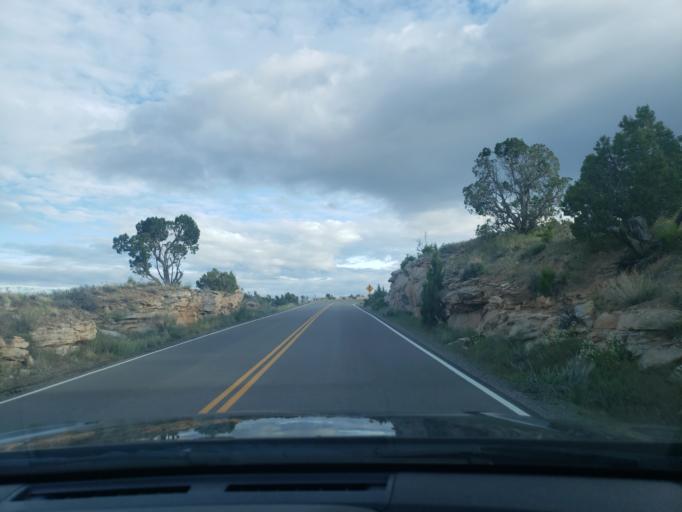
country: US
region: Colorado
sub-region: Mesa County
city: Redlands
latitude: 39.0339
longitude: -108.6472
